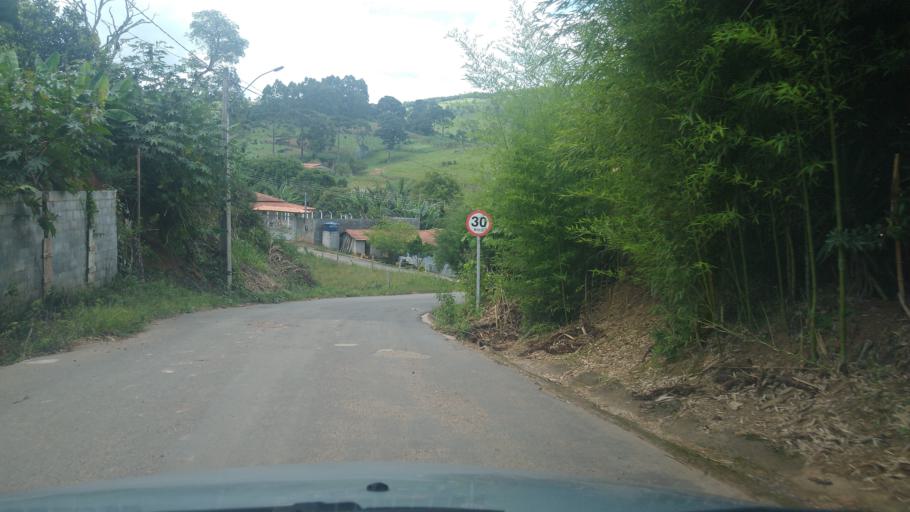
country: BR
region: Minas Gerais
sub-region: Extrema
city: Extrema
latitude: -22.7284
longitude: -46.3136
